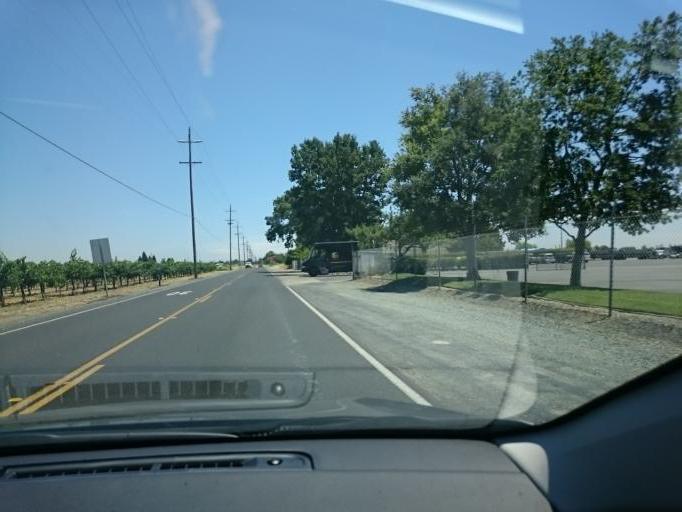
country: US
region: California
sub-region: San Joaquin County
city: Collierville
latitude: 38.1892
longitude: -121.2593
